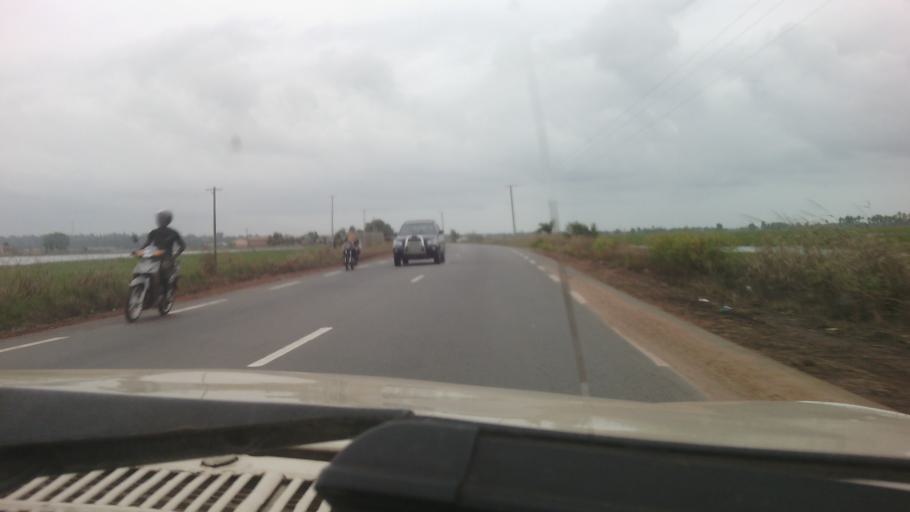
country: BJ
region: Mono
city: Come
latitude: 6.3947
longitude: 1.9292
